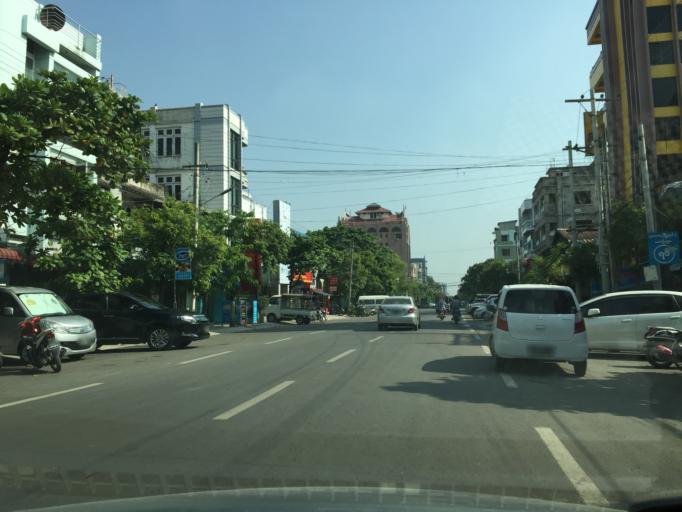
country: MM
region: Mandalay
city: Mandalay
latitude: 21.9716
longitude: 96.0789
